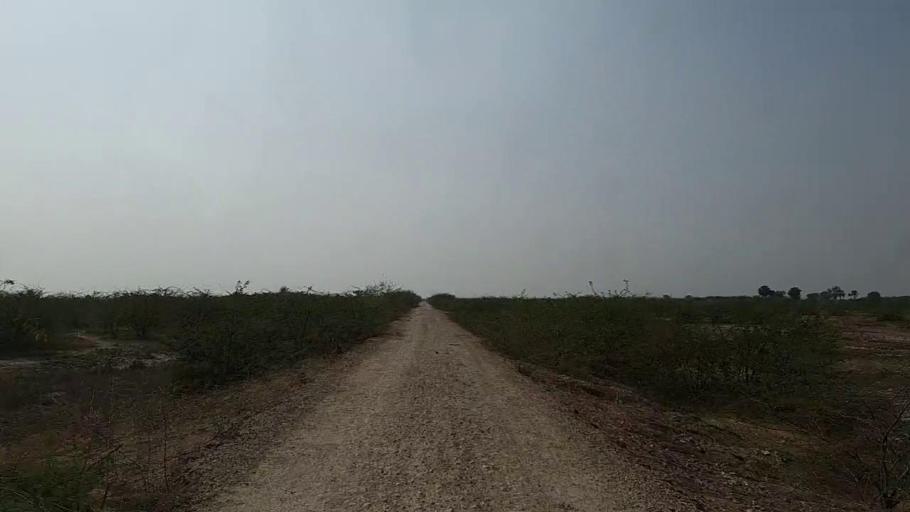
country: PK
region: Sindh
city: Naukot
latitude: 24.7606
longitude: 69.3183
